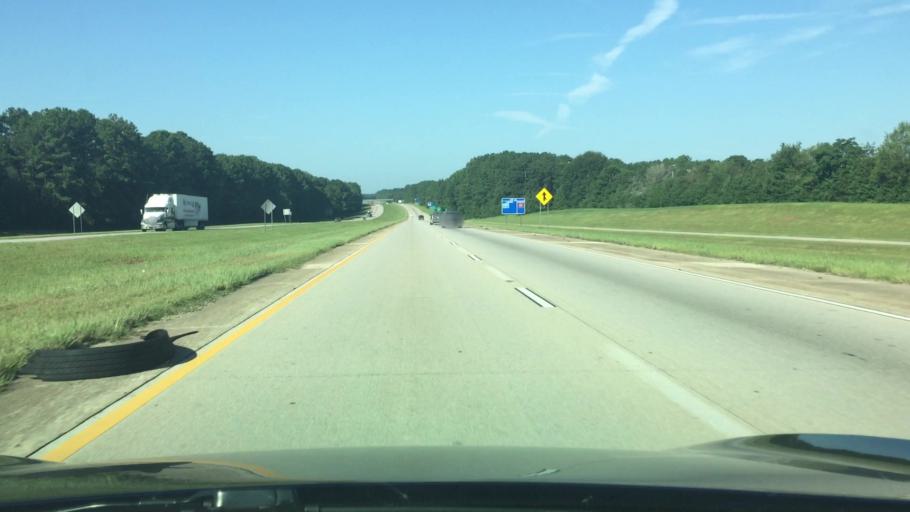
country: US
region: Georgia
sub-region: Troup County
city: La Grange
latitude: 32.9994
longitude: -85.0139
